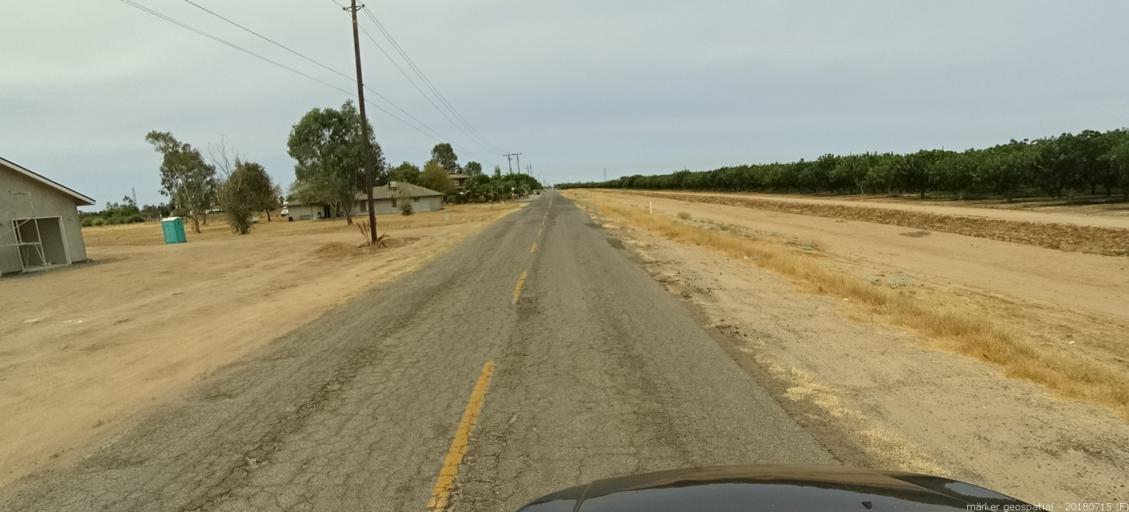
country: US
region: California
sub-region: Madera County
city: Madera Acres
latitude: 37.0255
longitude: -120.0821
